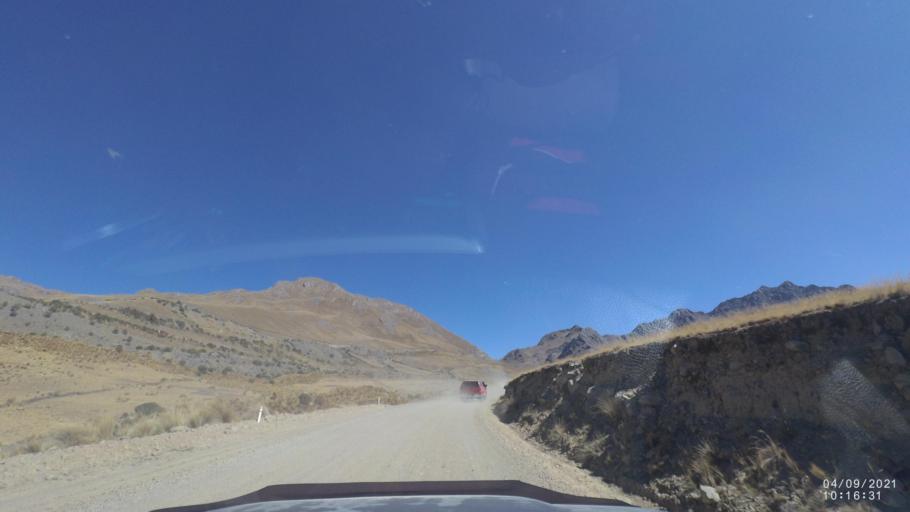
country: BO
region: Cochabamba
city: Sipe Sipe
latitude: -17.3215
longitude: -66.4189
